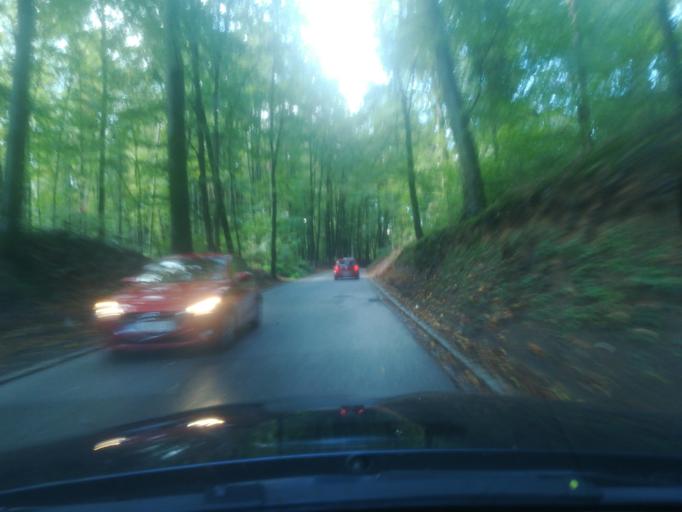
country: AT
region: Upper Austria
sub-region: Linz Stadt
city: Linz
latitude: 48.3339
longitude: 14.2838
